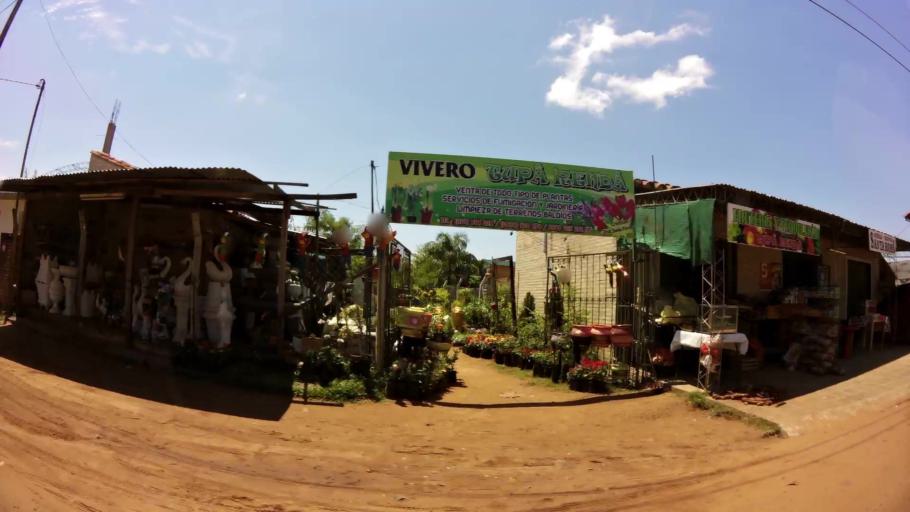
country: PY
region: Central
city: Nemby
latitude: -25.3992
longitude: -57.5336
